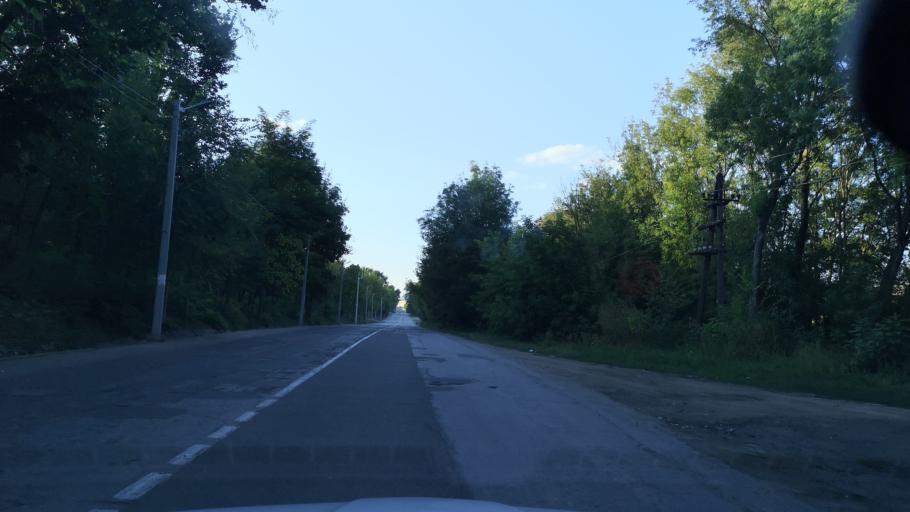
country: MD
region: Orhei
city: Orhei
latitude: 47.3951
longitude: 28.8214
